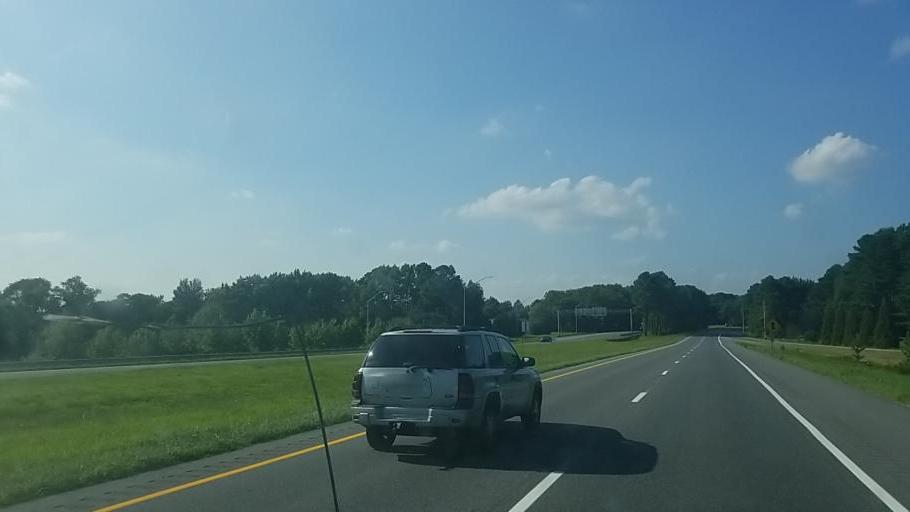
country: US
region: Maryland
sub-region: Worcester County
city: Berlin
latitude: 38.3444
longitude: -75.2138
